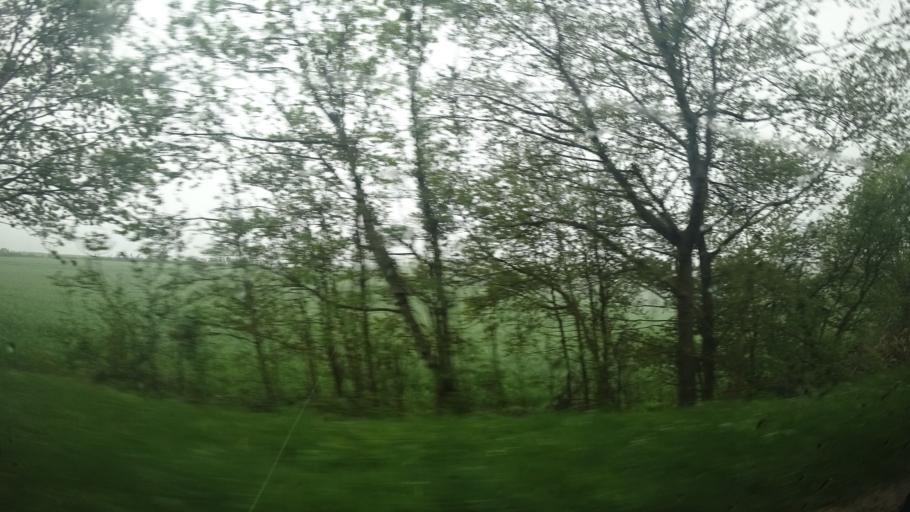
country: FR
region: Midi-Pyrenees
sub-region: Departement de l'Aveyron
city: Laissac
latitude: 44.3271
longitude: 2.7871
